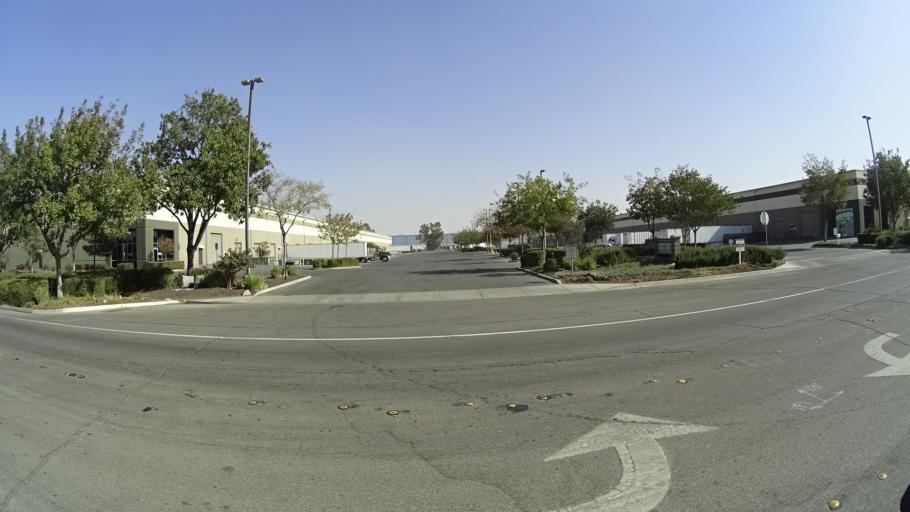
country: US
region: California
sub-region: Yolo County
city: Woodland
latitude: 38.6884
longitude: -121.7469
